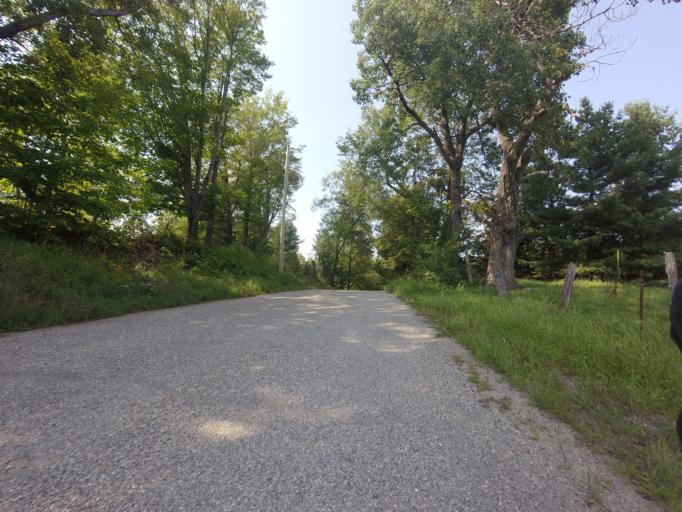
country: CA
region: Ontario
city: Skatepark
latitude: 44.7427
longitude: -76.8283
